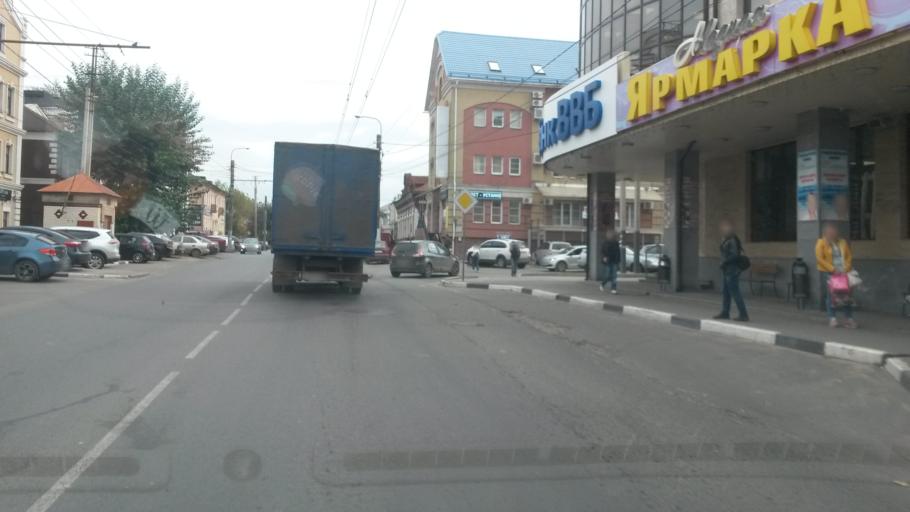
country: RU
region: Ivanovo
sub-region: Gorod Ivanovo
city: Ivanovo
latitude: 56.9936
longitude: 40.9823
